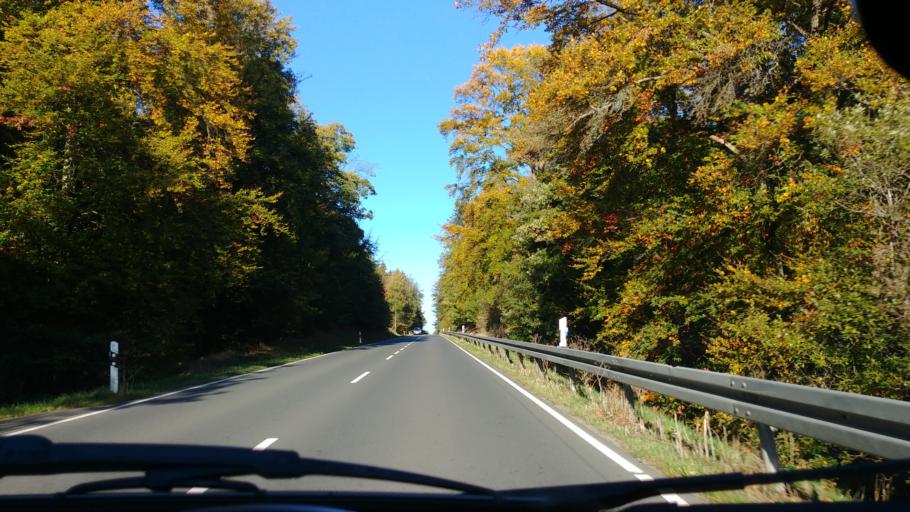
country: DE
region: Rheinland-Pfalz
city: Reckenroth
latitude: 50.1750
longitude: 7.9986
